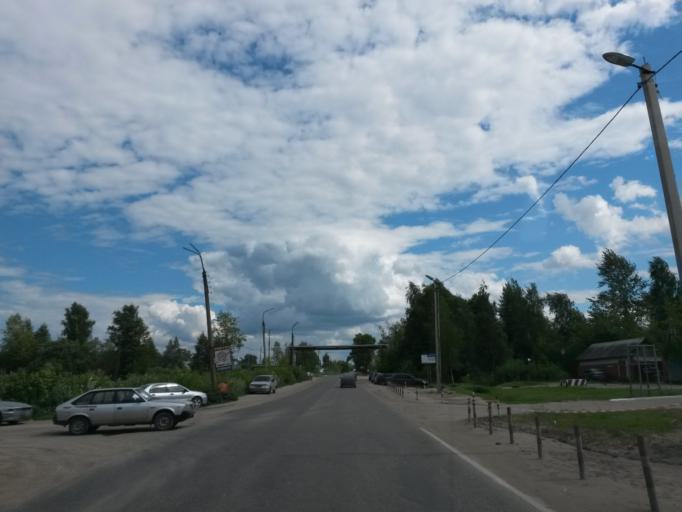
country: RU
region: Ivanovo
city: Novo-Talitsy
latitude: 57.0043
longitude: 40.8823
